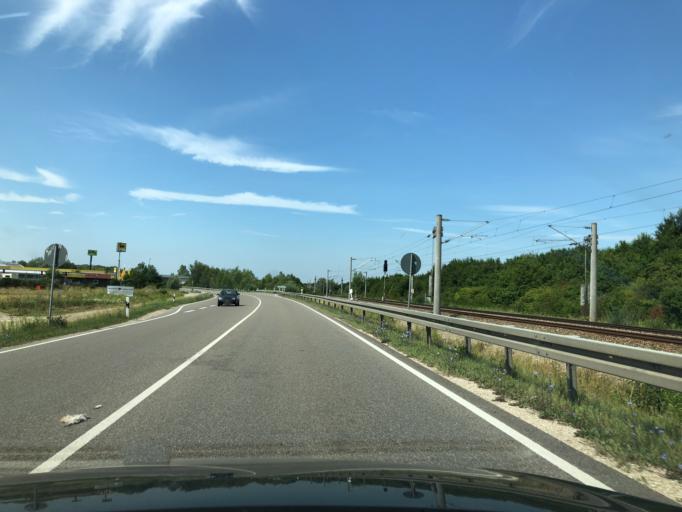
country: DE
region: Bavaria
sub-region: Upper Bavaria
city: Karlskron
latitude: 48.7070
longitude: 11.4233
